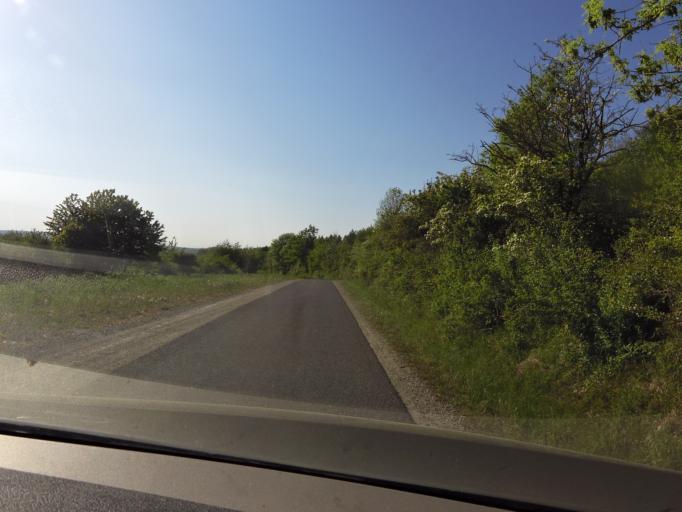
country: DE
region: Thuringia
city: Lauterbach
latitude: 51.0737
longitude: 10.3687
